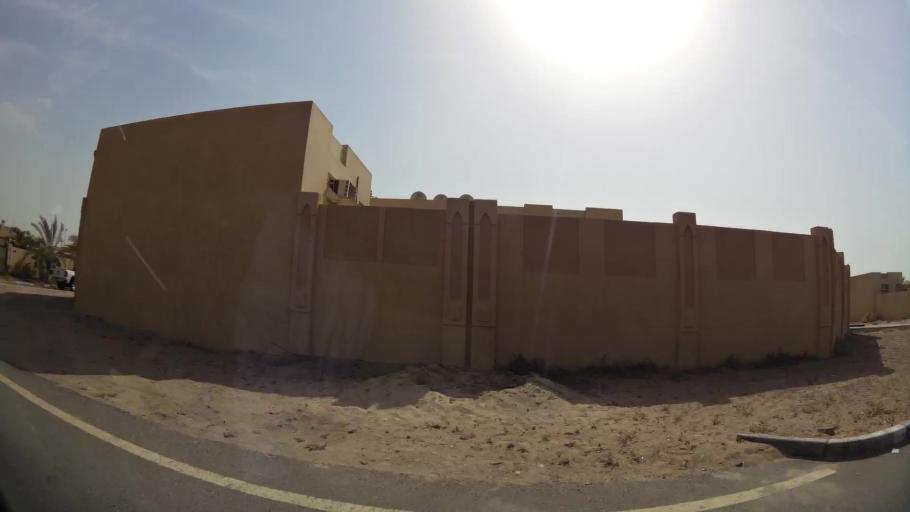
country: AE
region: Ash Shariqah
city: Sharjah
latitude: 25.2585
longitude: 55.4317
